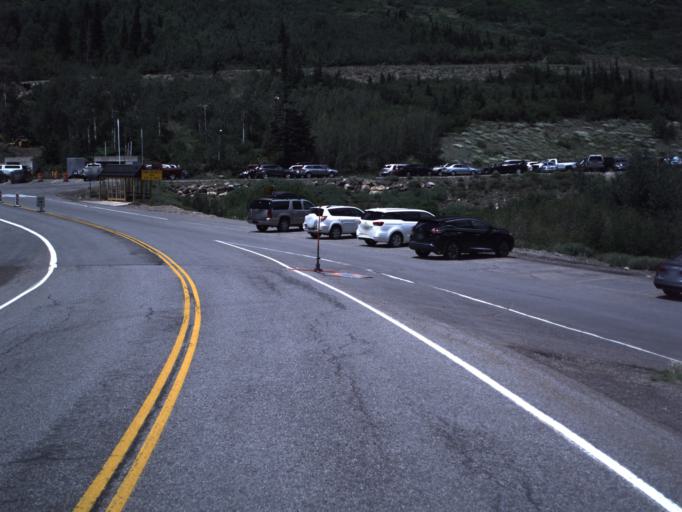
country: US
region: Utah
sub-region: Salt Lake County
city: Granite
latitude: 40.5831
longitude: -111.6528
